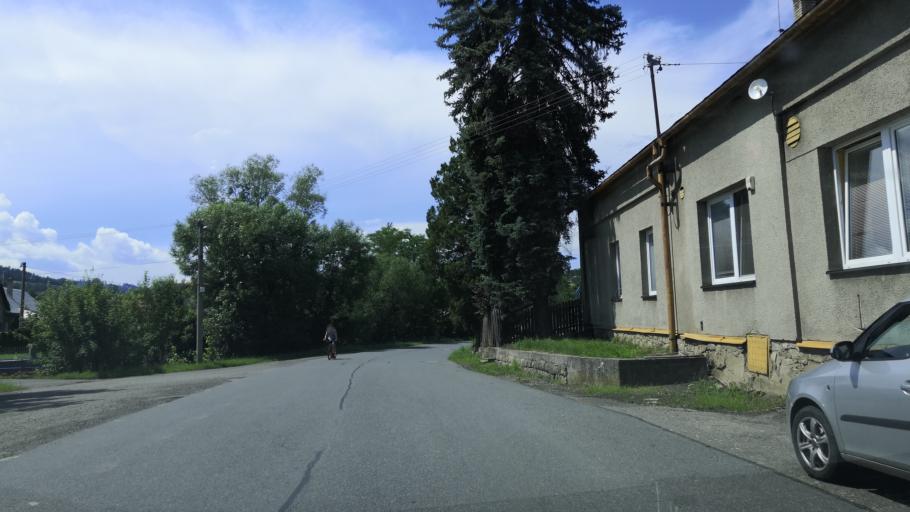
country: CZ
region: Zlin
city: Vidce
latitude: 49.4416
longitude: 18.0944
